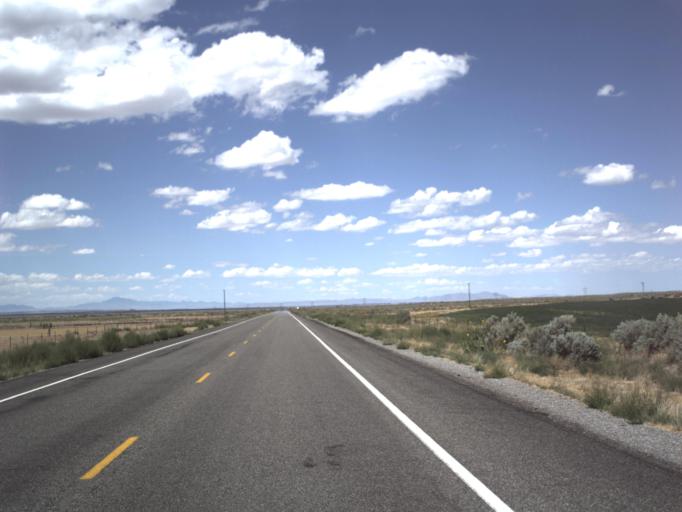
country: US
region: Utah
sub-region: Millard County
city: Fillmore
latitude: 39.1410
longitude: -112.3759
